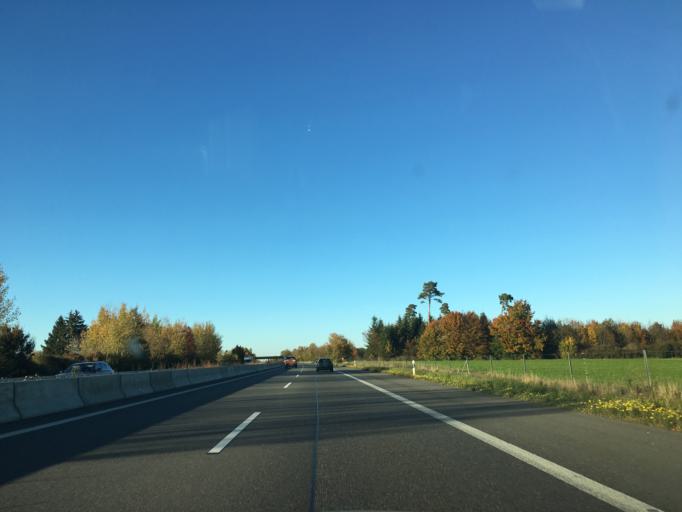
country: DE
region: Baden-Wuerttemberg
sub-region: Freiburg Region
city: Zimmern ob Rottweil
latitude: 48.1542
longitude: 8.5731
